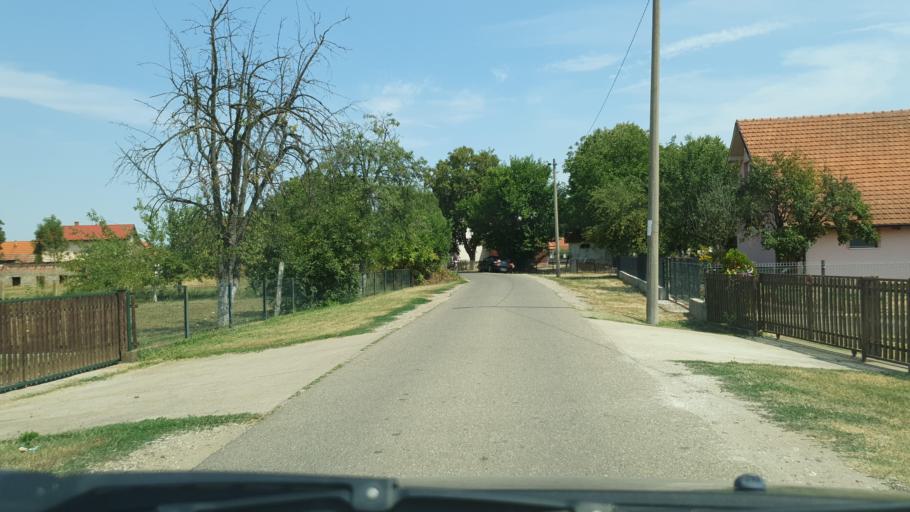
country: BA
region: Republika Srpska
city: Bijeljina
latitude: 44.7246
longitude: 19.2053
